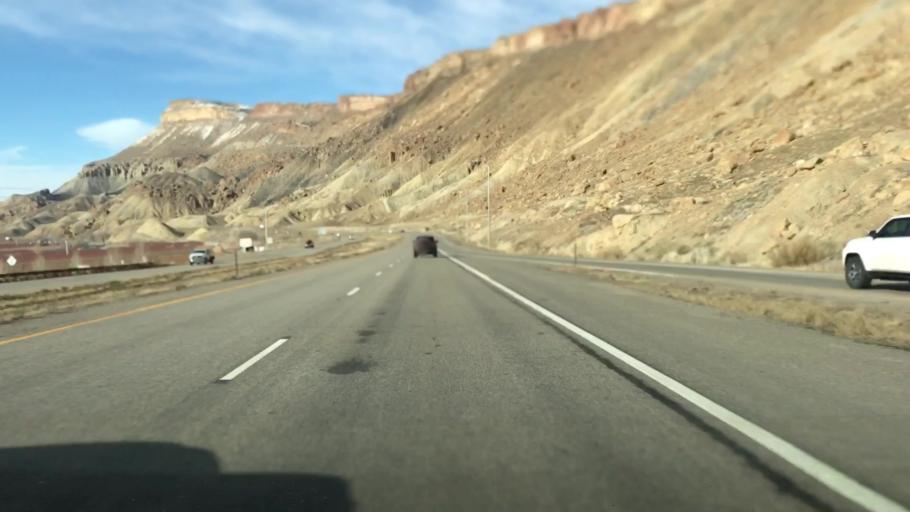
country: US
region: Colorado
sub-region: Mesa County
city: Palisade
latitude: 39.1185
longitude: -108.3613
